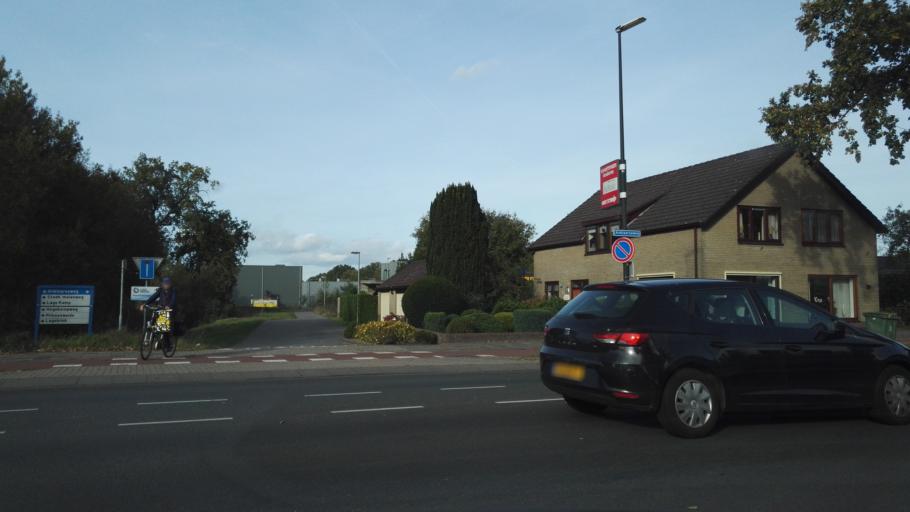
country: NL
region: Gelderland
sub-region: Gemeente Apeldoorn
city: Apeldoorn
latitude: 52.2351
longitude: 5.9738
